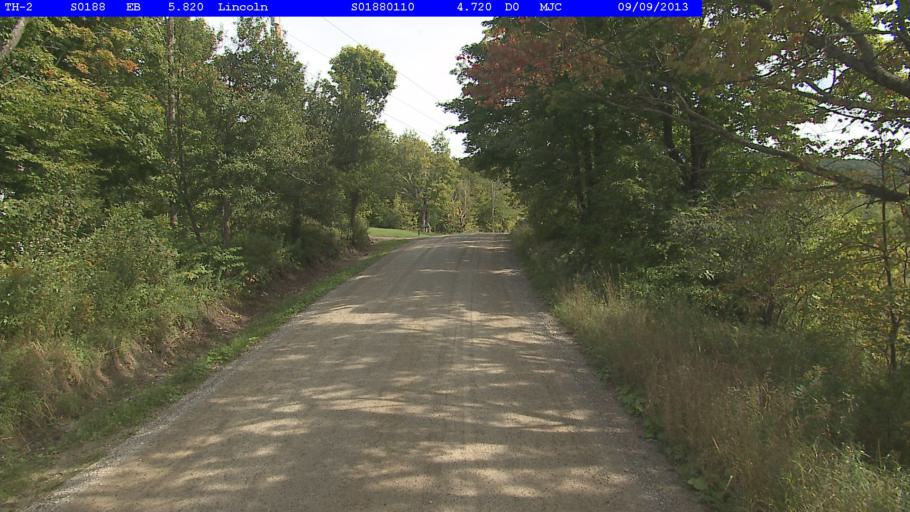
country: US
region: Vermont
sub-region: Addison County
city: Bristol
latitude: 44.0934
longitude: -72.9588
